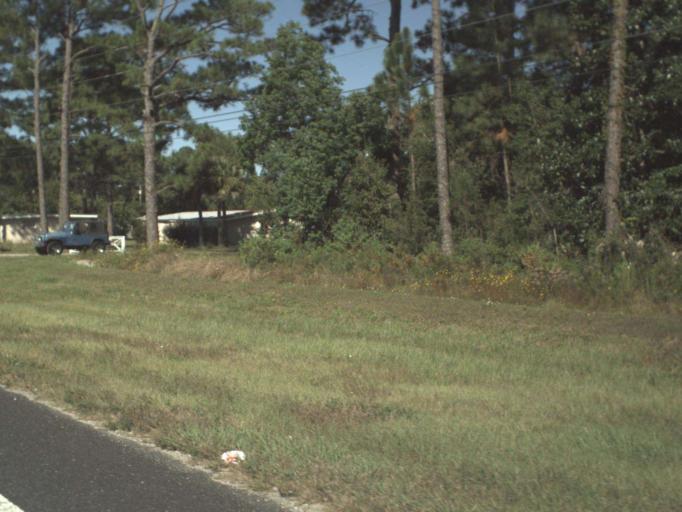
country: US
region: Florida
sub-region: Walton County
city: Miramar Beach
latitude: 30.3749
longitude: -86.2667
